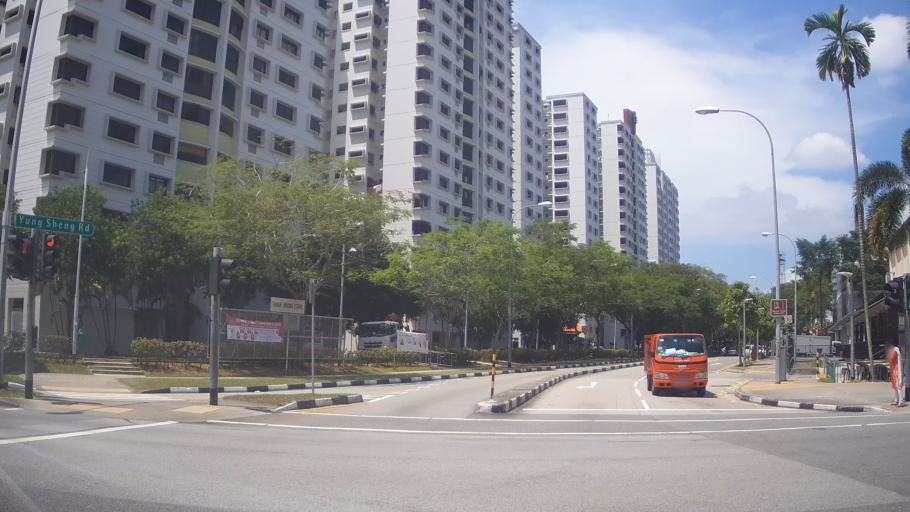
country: SG
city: Singapore
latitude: 1.3343
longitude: 103.7227
